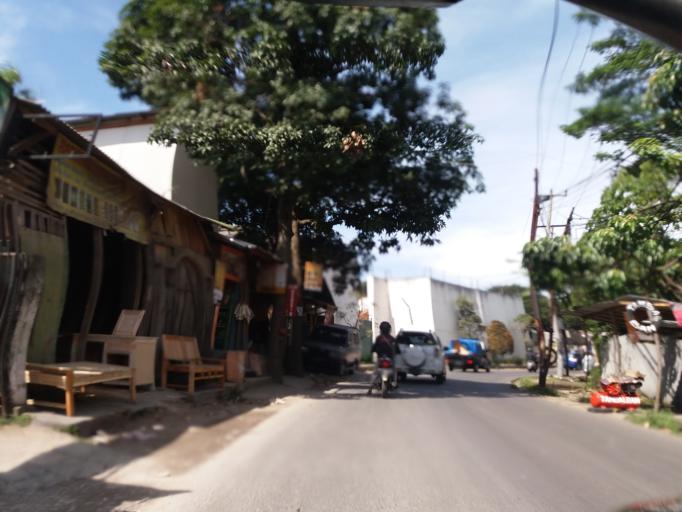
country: ID
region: West Java
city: Margahayukencana
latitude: -6.9523
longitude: 107.5798
